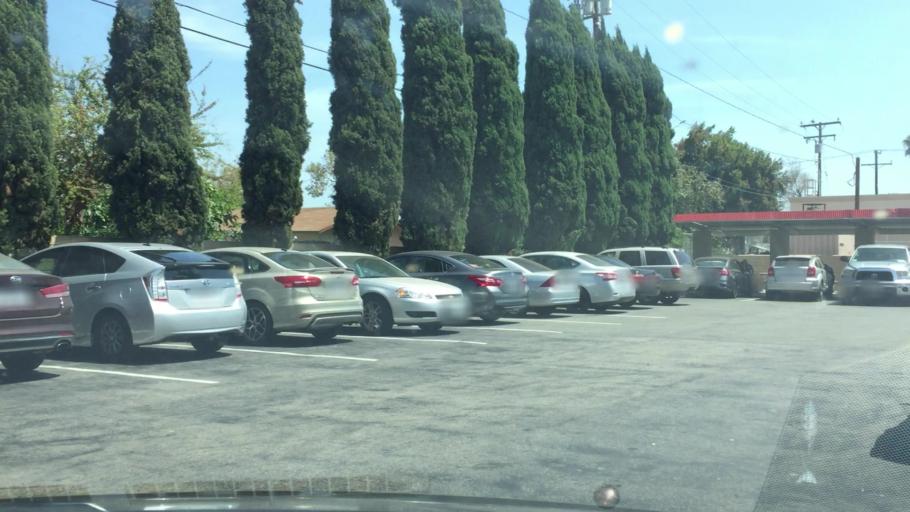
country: US
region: California
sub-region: Orange County
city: Santa Ana
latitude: 33.7524
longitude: -117.8847
